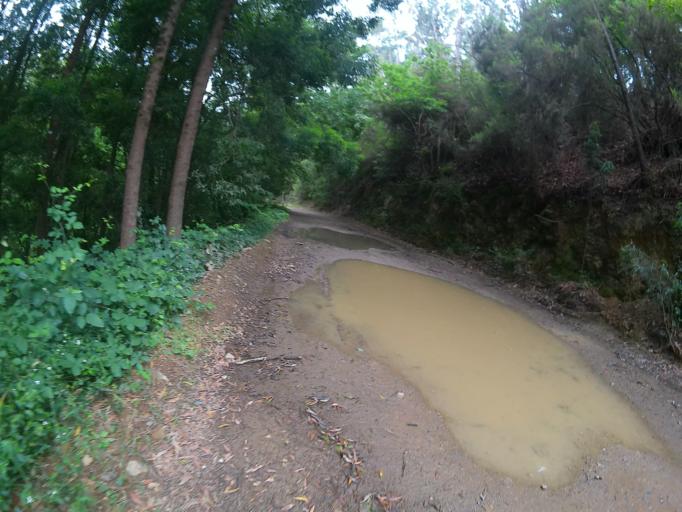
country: PT
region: Aveiro
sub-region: Albergaria-A-Velha
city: Branca
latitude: 40.7684
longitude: -8.4422
